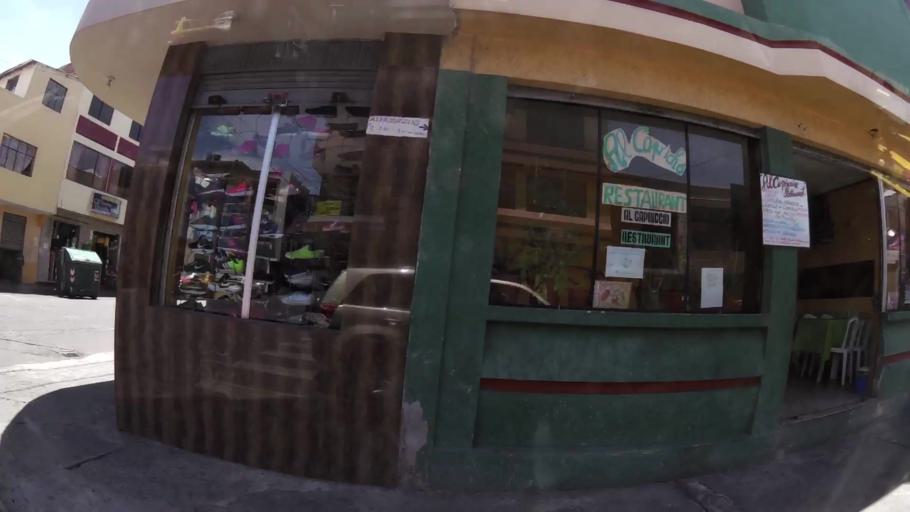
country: EC
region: Chimborazo
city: Riobamba
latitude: -1.6693
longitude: -78.6461
